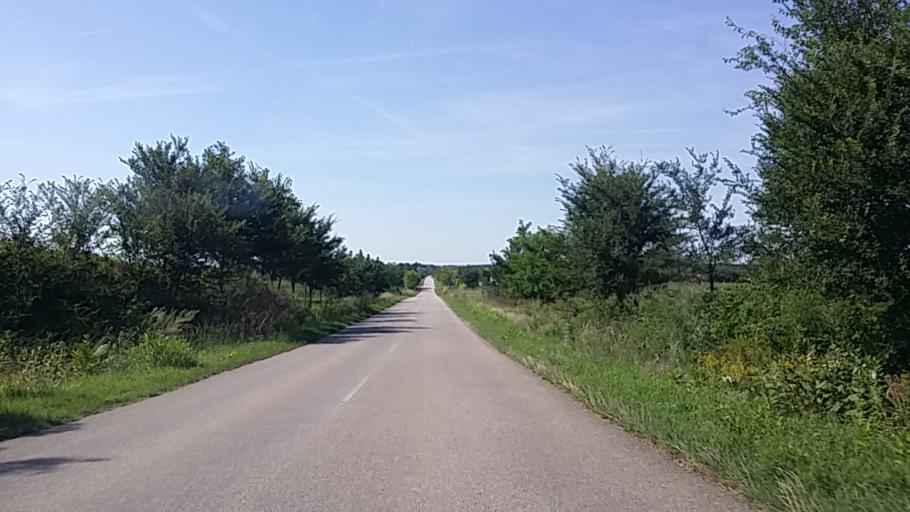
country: HU
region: Fejer
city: Deg
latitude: 46.8850
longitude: 18.4479
